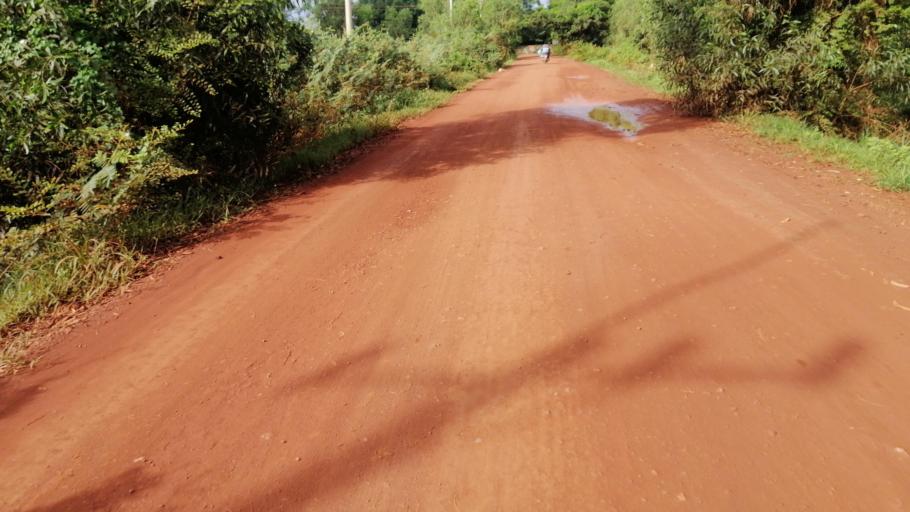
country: KH
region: Siem Reap
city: Siem Reap
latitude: 13.3597
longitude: 103.8289
